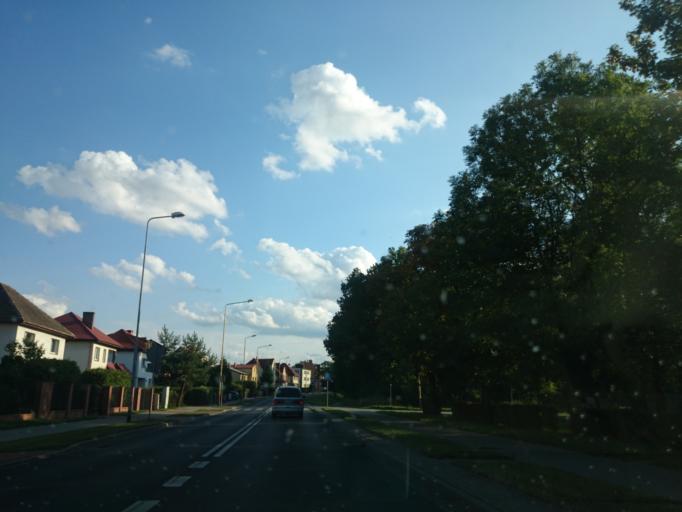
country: PL
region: West Pomeranian Voivodeship
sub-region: Powiat pyrzycki
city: Pyrzyce
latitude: 53.1361
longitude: 14.8936
